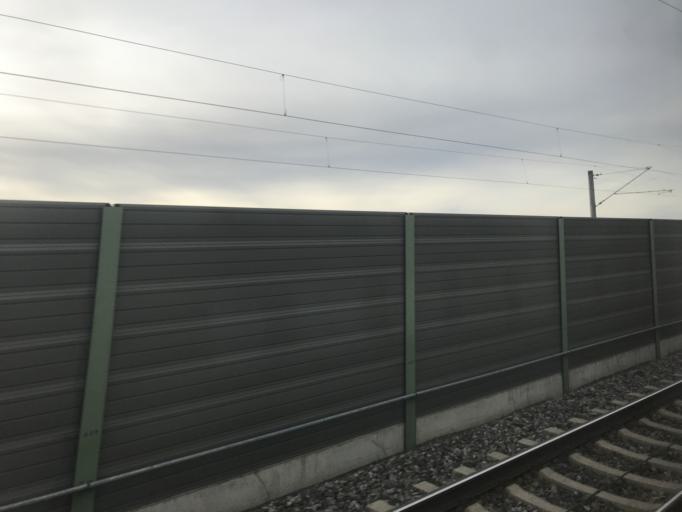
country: DE
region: Bavaria
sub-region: Swabia
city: Mering
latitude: 48.2685
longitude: 10.9788
